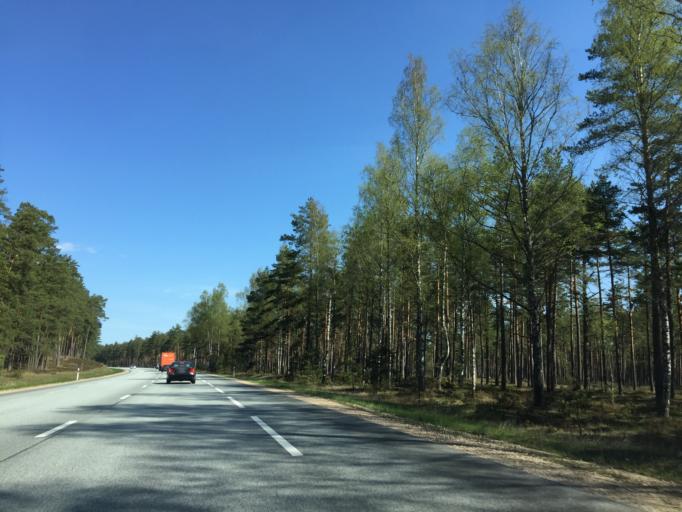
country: LV
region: Carnikava
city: Carnikava
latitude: 57.1568
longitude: 24.3461
